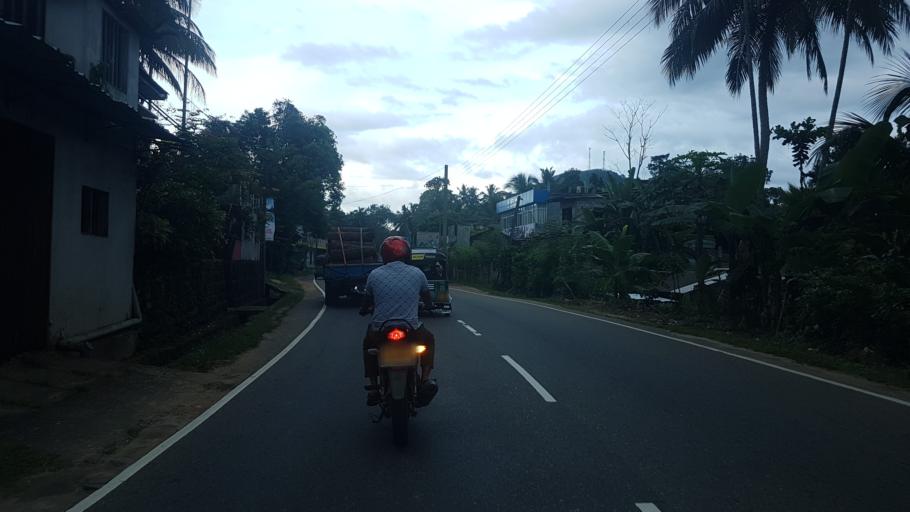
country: LK
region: Western
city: Hanwella Ihala
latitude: 7.0143
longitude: 80.2631
